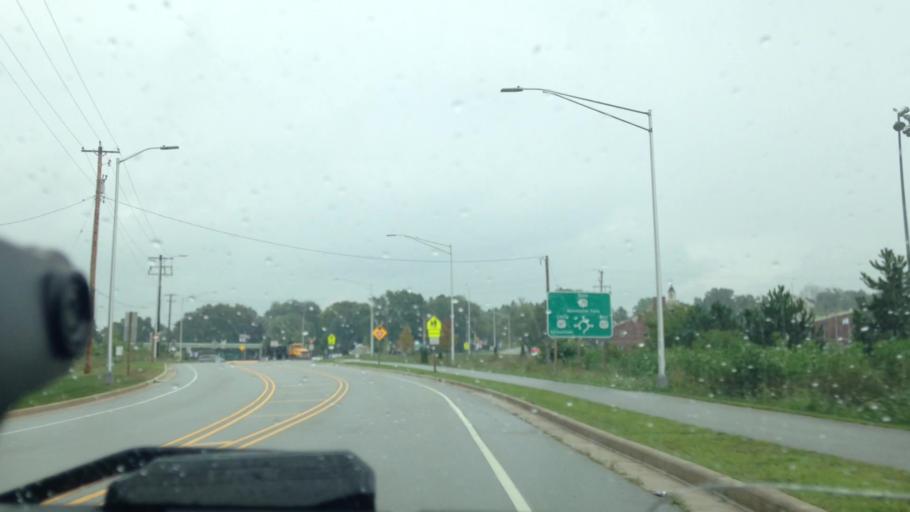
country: US
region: Wisconsin
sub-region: Washington County
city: Richfield
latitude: 43.2521
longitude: -88.1920
